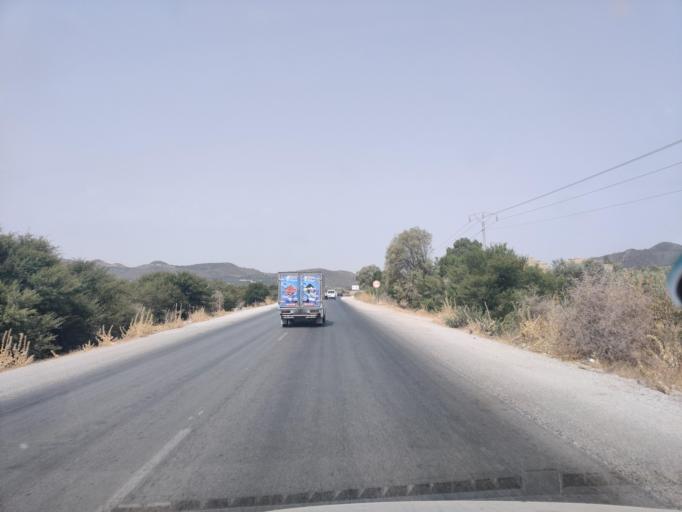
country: TN
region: Tunis
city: Hammam-Lif
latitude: 36.6188
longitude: 10.4137
